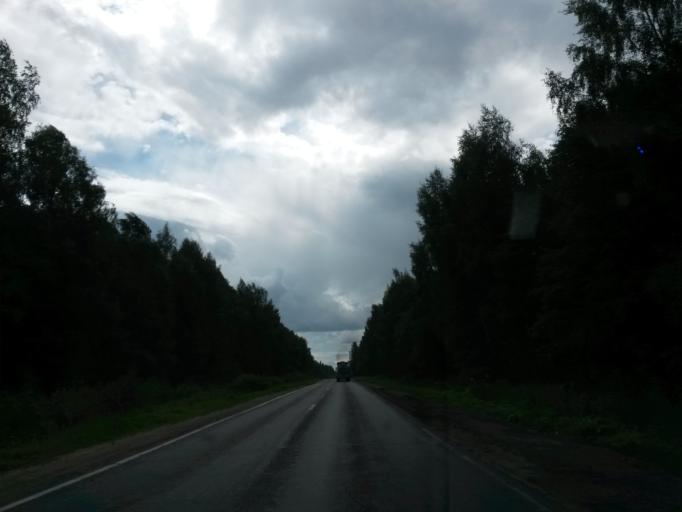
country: RU
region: Jaroslavl
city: Yaroslavl
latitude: 57.5028
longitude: 39.8989
